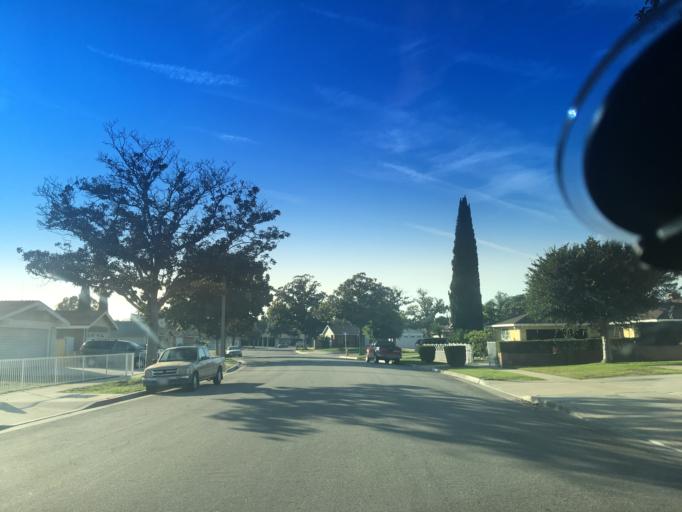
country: US
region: California
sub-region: Orange County
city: Anaheim
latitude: 33.8200
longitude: -117.8916
